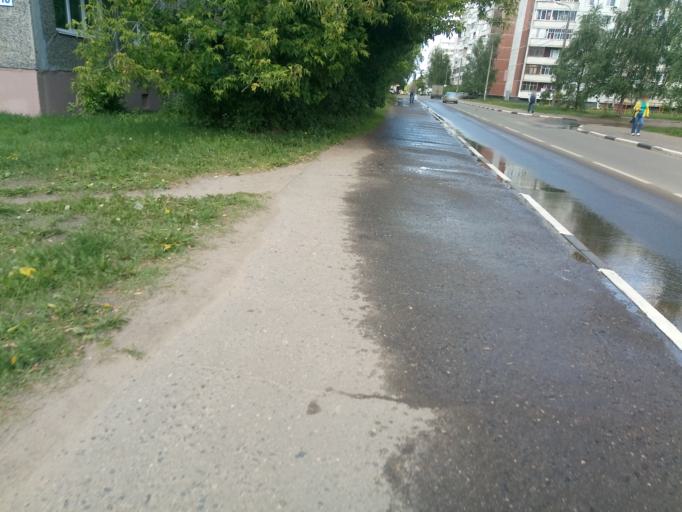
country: RU
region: Jaroslavl
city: Yaroslavl
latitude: 57.6535
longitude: 39.9613
